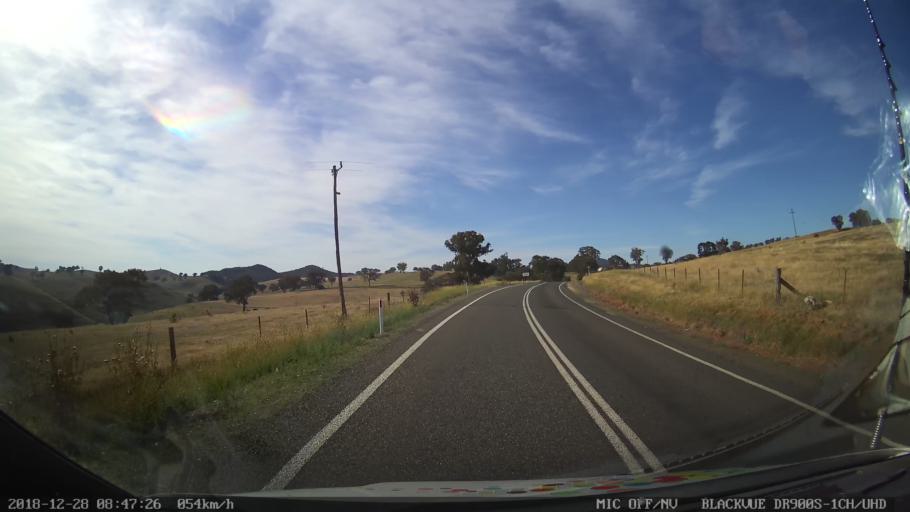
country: AU
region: New South Wales
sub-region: Upper Lachlan Shire
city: Crookwell
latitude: -34.0283
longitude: 149.3344
